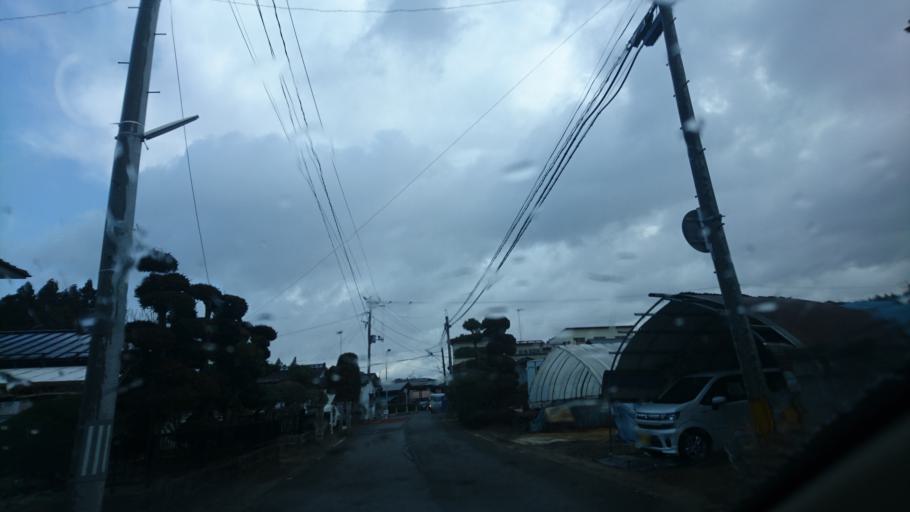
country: JP
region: Iwate
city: Ichinoseki
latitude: 38.7693
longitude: 141.0351
